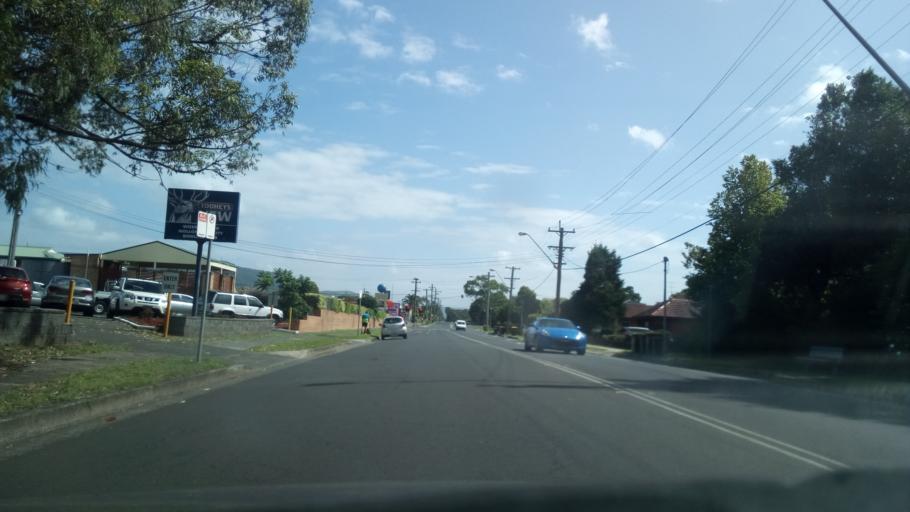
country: AU
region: New South Wales
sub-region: Wollongong
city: Gwynneville
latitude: -34.4177
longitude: 150.8849
